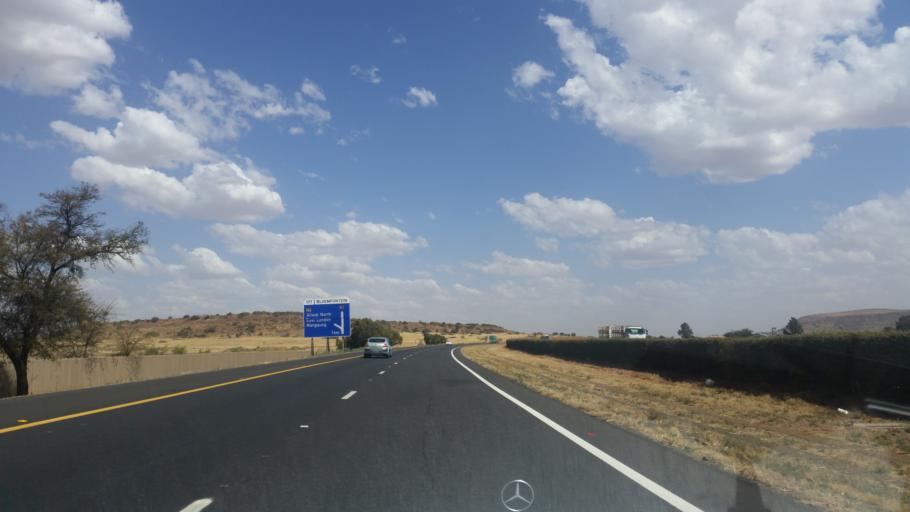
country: ZA
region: Orange Free State
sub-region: Mangaung Metropolitan Municipality
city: Bloemfontein
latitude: -29.1876
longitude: 26.1932
